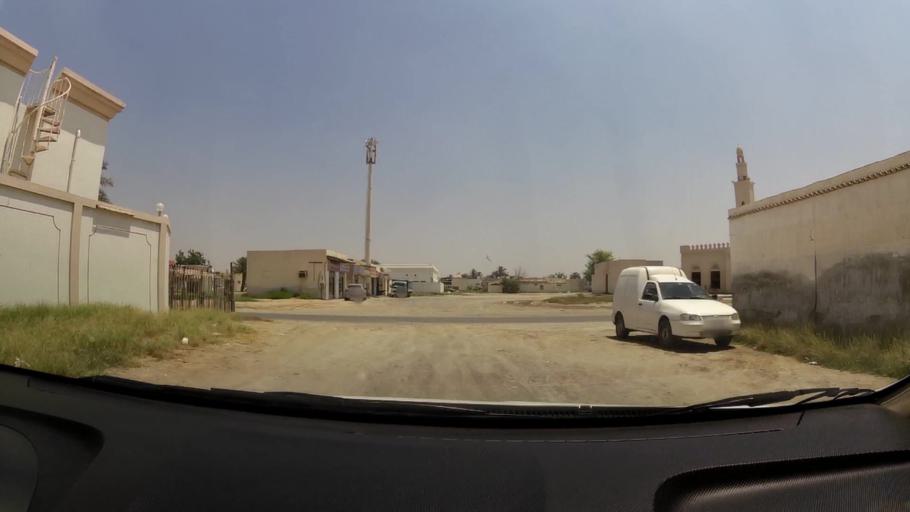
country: AE
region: Umm al Qaywayn
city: Umm al Qaywayn
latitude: 25.5568
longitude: 55.5580
